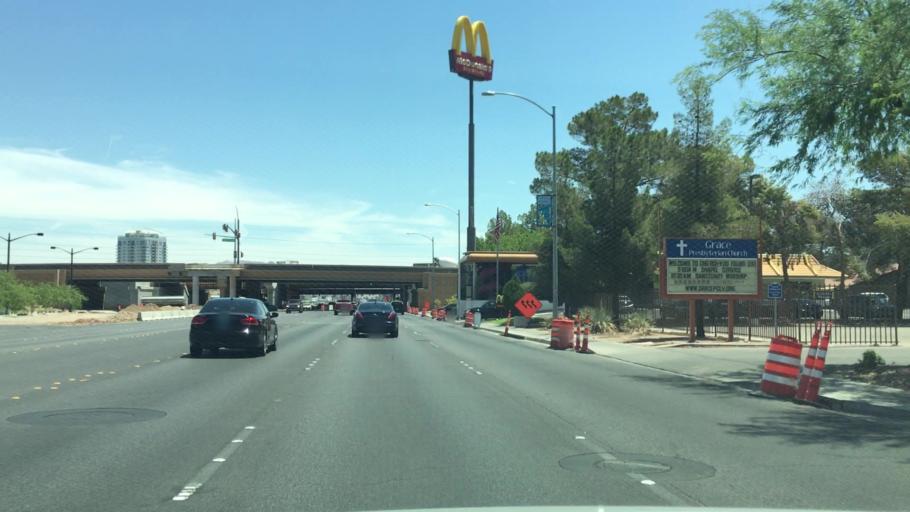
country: US
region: Nevada
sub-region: Clark County
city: Las Vegas
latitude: 36.1588
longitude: -115.1636
